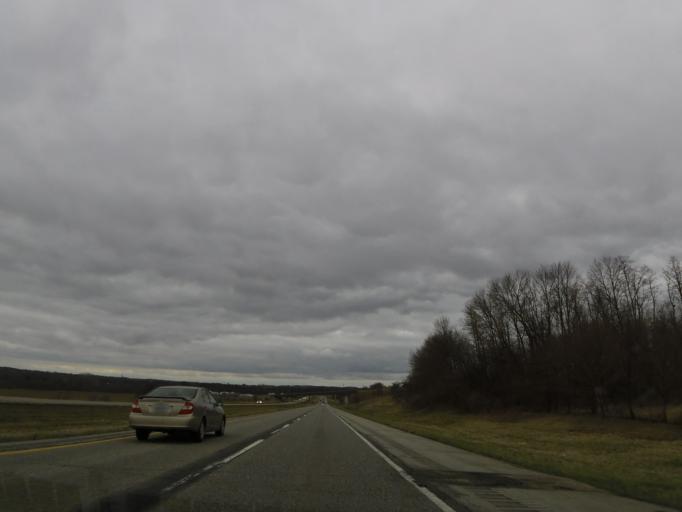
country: US
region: Iowa
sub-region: Benton County
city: Urbana
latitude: 42.2073
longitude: -91.8361
